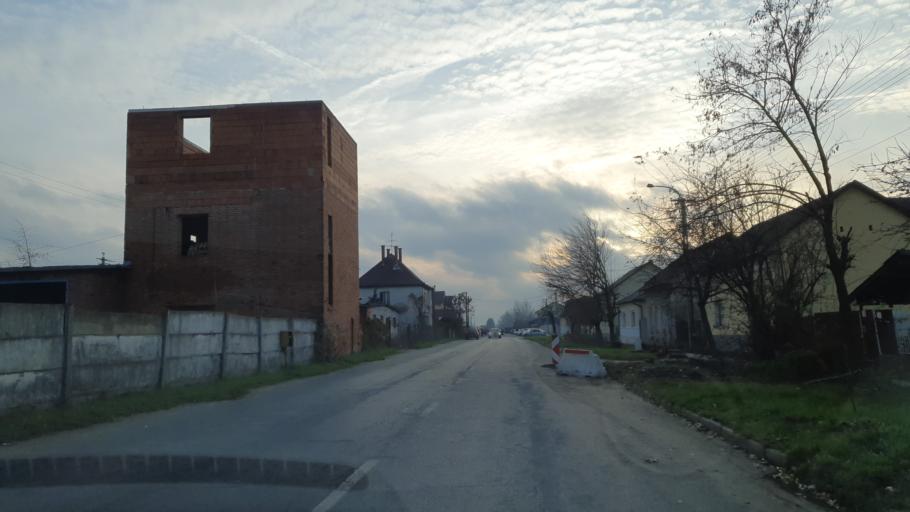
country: HU
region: Szabolcs-Szatmar-Bereg
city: Kisvarda
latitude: 48.2098
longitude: 22.0796
